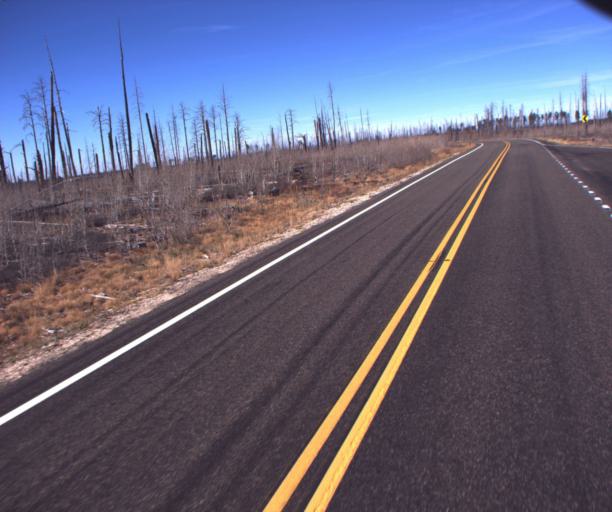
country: US
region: Arizona
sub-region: Coconino County
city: Fredonia
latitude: 36.5848
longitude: -112.1757
